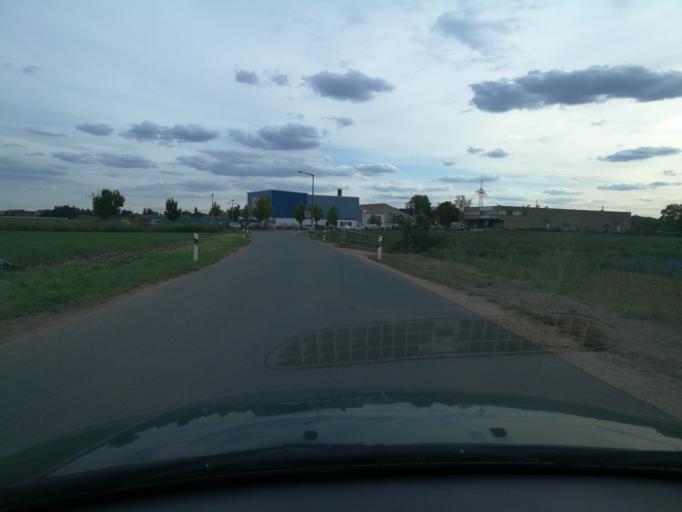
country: DE
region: Bavaria
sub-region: Regierungsbezirk Mittelfranken
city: Furth
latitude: 49.5054
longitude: 11.0043
